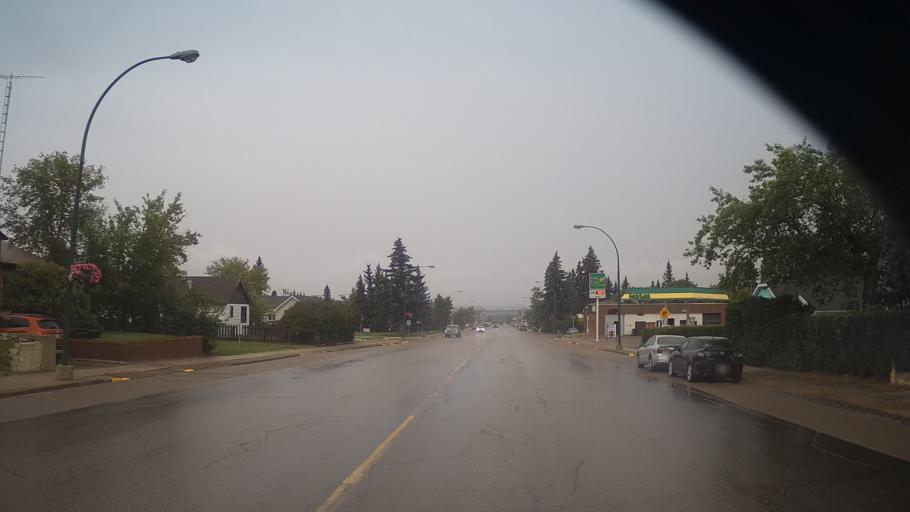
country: CA
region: Saskatchewan
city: Biggar
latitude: 52.0596
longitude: -107.9826
